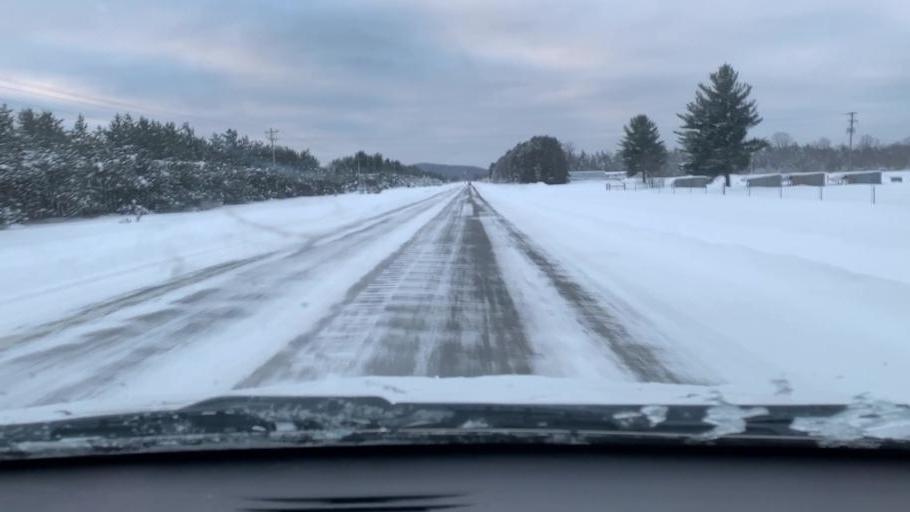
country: US
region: Michigan
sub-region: Antrim County
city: Mancelona
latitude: 44.9279
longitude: -85.0509
